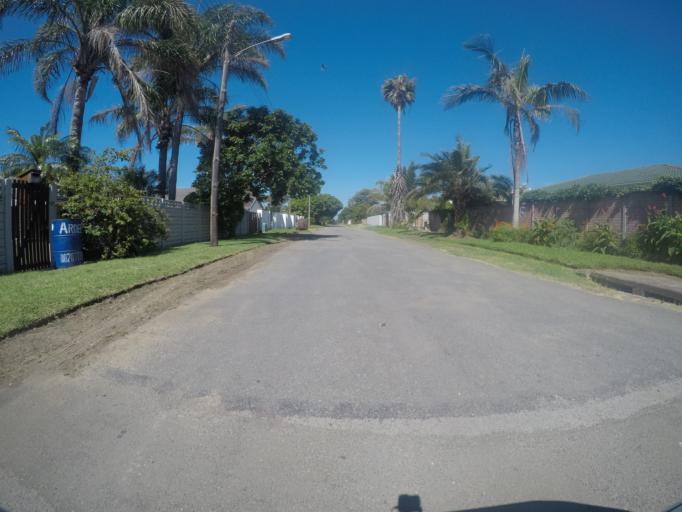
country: ZA
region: Eastern Cape
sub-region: Buffalo City Metropolitan Municipality
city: East London
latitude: -32.9490
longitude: 28.0069
